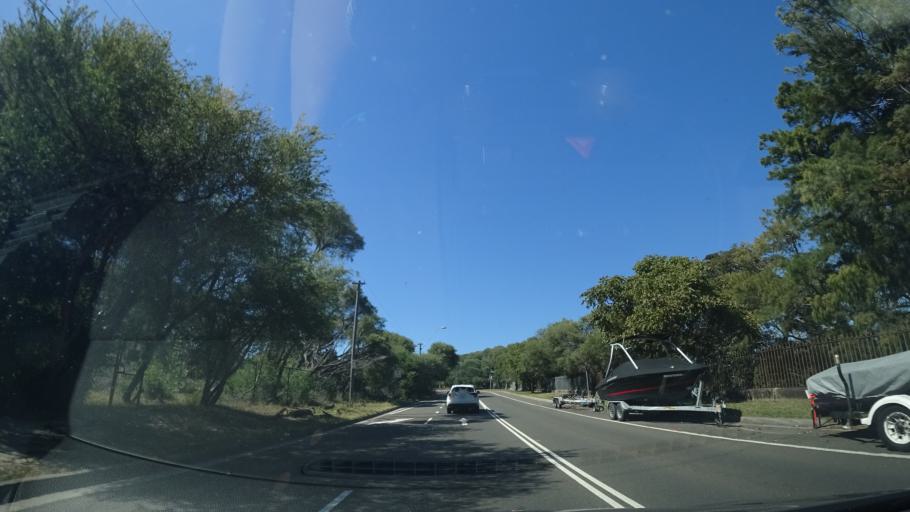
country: AU
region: New South Wales
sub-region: Waverley
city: Bondi Junction
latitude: -33.8993
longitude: 151.2422
